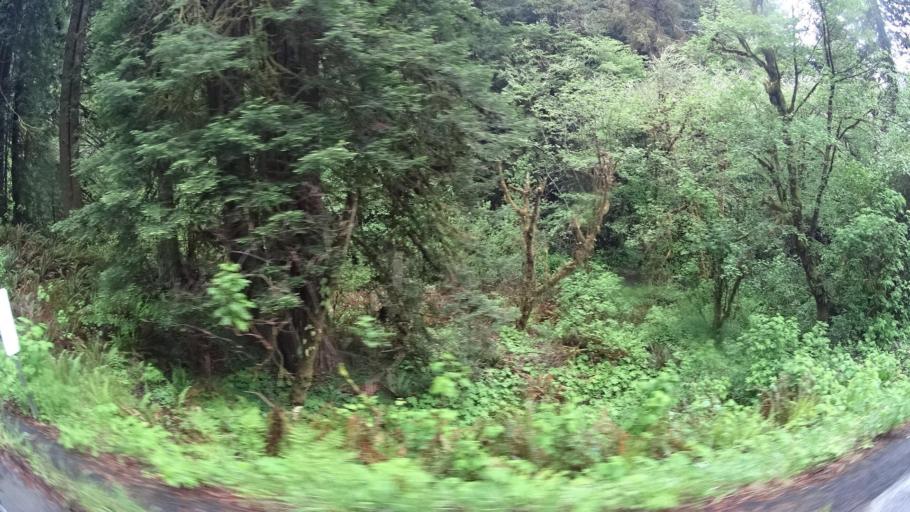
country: US
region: California
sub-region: Humboldt County
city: Bayside
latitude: 40.8140
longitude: -124.0257
